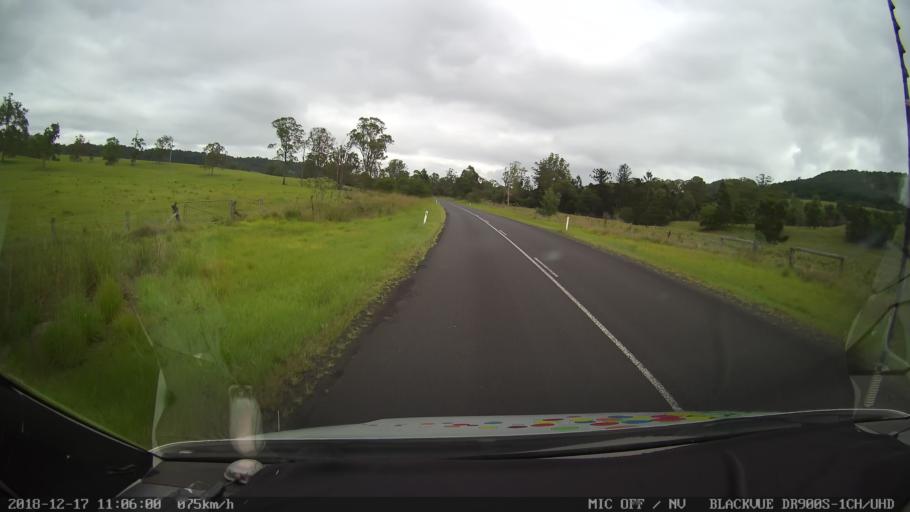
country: AU
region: New South Wales
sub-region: Kyogle
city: Kyogle
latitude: -28.7846
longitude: 152.6482
